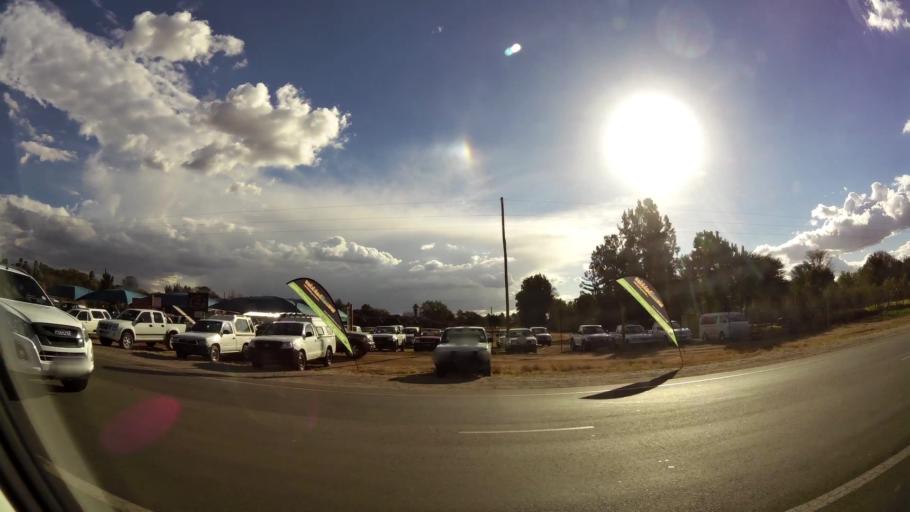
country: ZA
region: Limpopo
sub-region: Capricorn District Municipality
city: Polokwane
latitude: -23.9317
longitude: 29.4500
